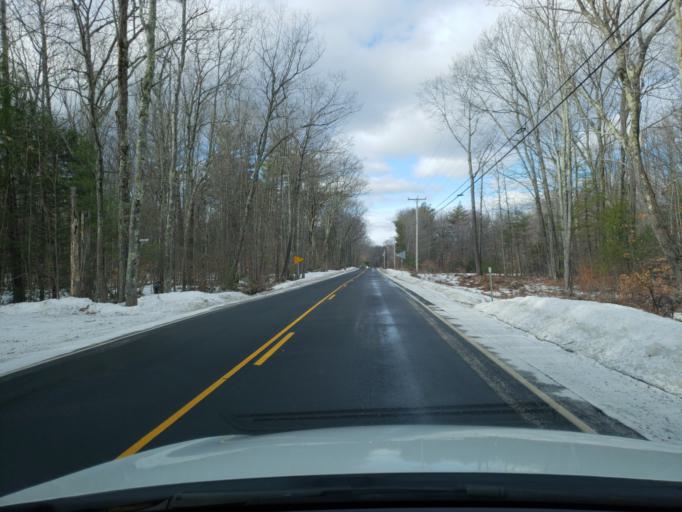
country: US
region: New Hampshire
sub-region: Hillsborough County
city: Deering
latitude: 43.0120
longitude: -71.8541
